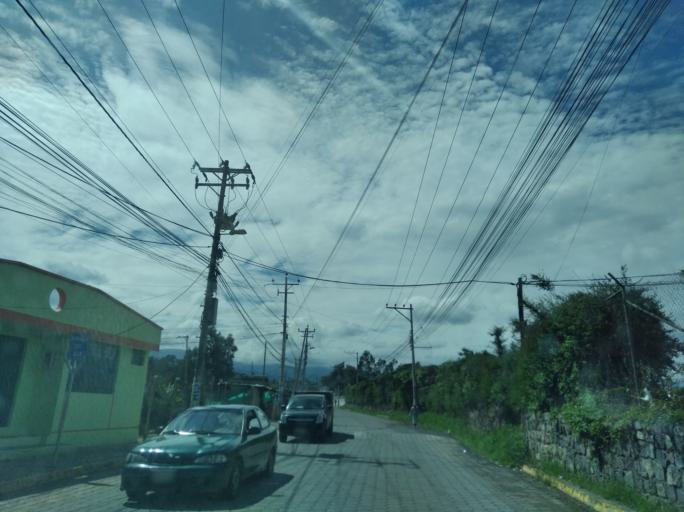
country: EC
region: Pichincha
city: Sangolqui
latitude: -0.2171
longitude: -78.3398
